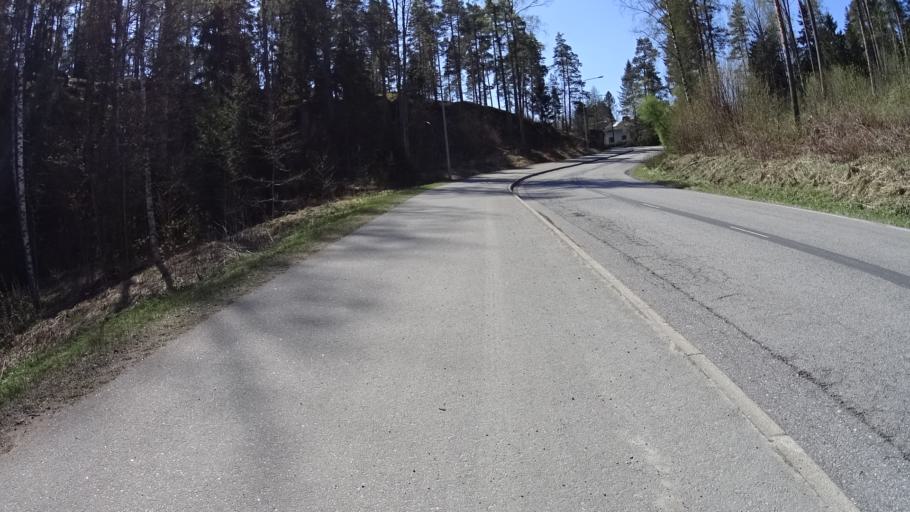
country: FI
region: Uusimaa
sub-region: Helsinki
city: Espoo
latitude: 60.2459
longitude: 24.6540
